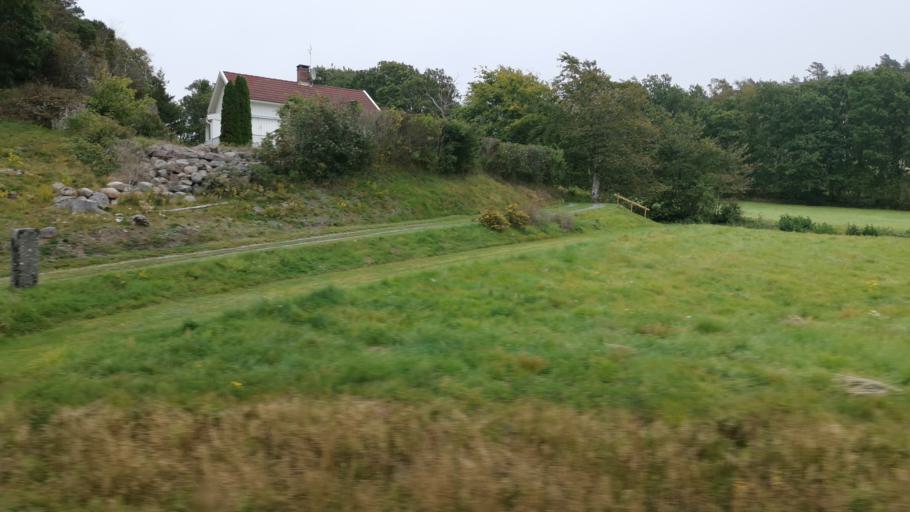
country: SE
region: Vaestra Goetaland
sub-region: Tanums Kommun
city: Tanumshede
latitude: 58.5930
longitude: 11.3663
